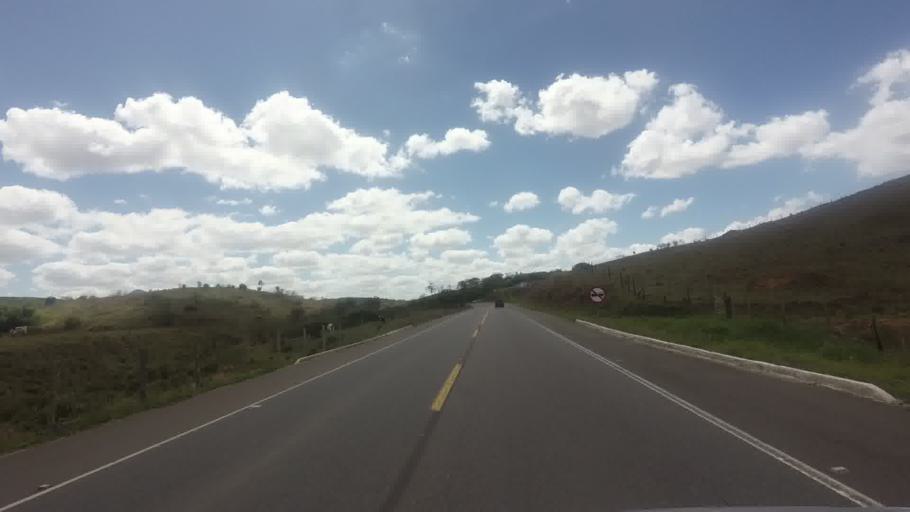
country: BR
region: Minas Gerais
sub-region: Recreio
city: Recreio
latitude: -21.6641
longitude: -42.3805
